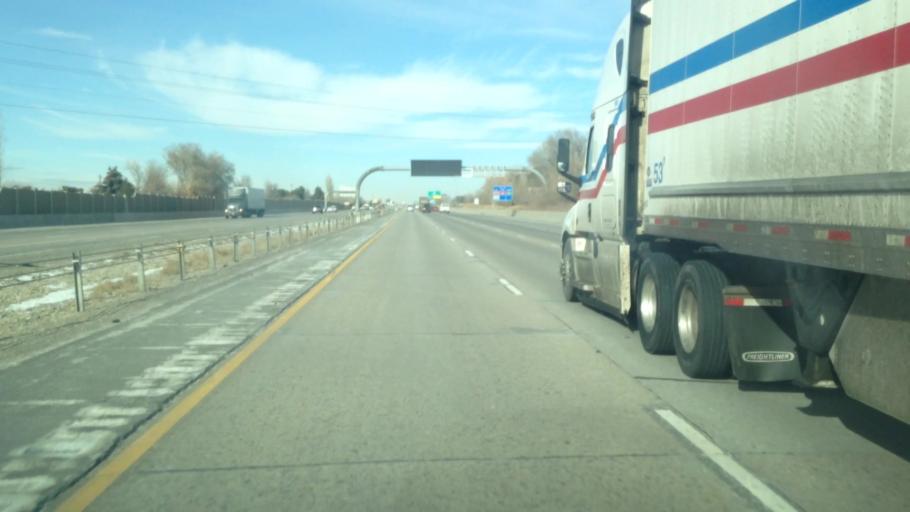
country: US
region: Utah
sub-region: Davis County
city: Hill Air Force Bace
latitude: 41.0959
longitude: -111.9969
